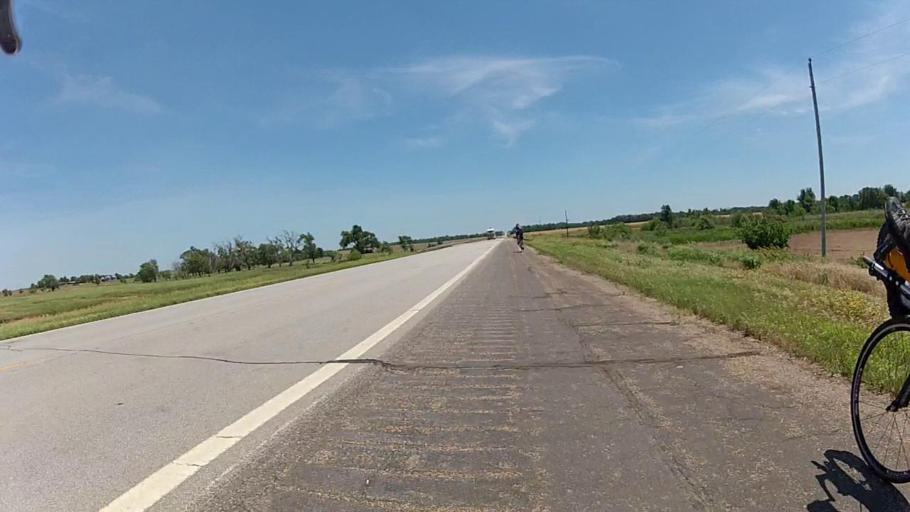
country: US
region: Kansas
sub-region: Barber County
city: Medicine Lodge
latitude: 37.2533
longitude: -98.3165
